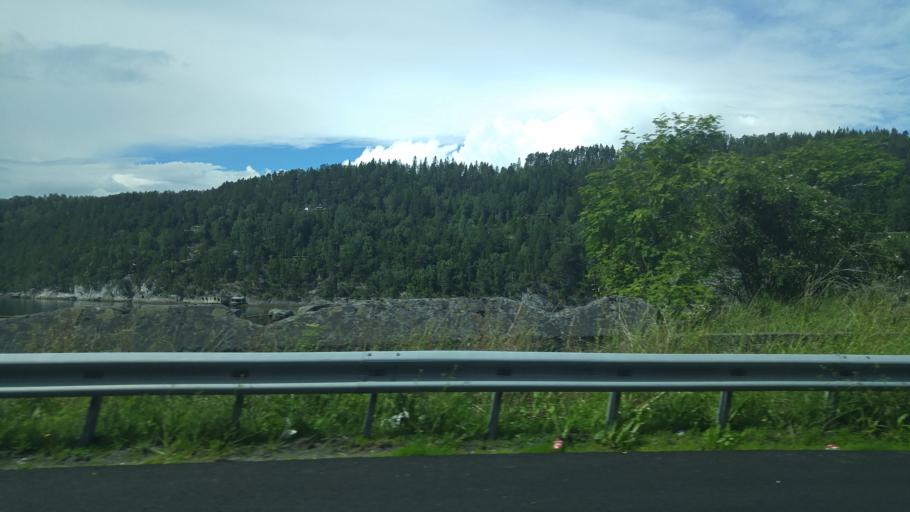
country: NO
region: Nord-Trondelag
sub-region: Stjordal
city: Stjordalshalsen
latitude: 63.5607
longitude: 10.9341
